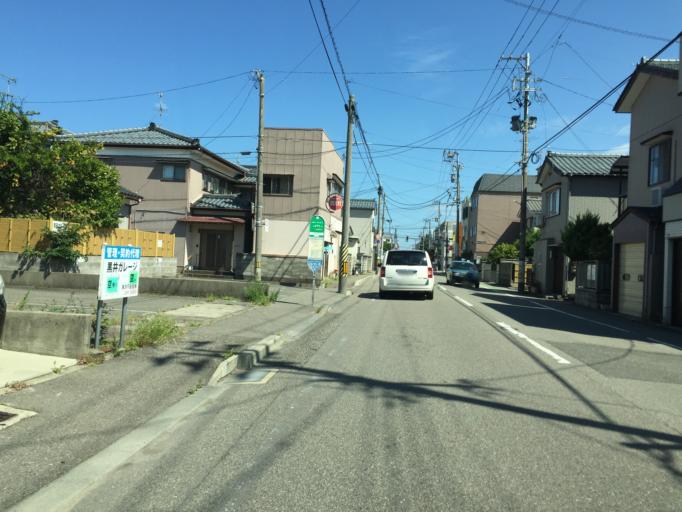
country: JP
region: Niigata
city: Niigata-shi
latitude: 37.9336
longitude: 139.0531
